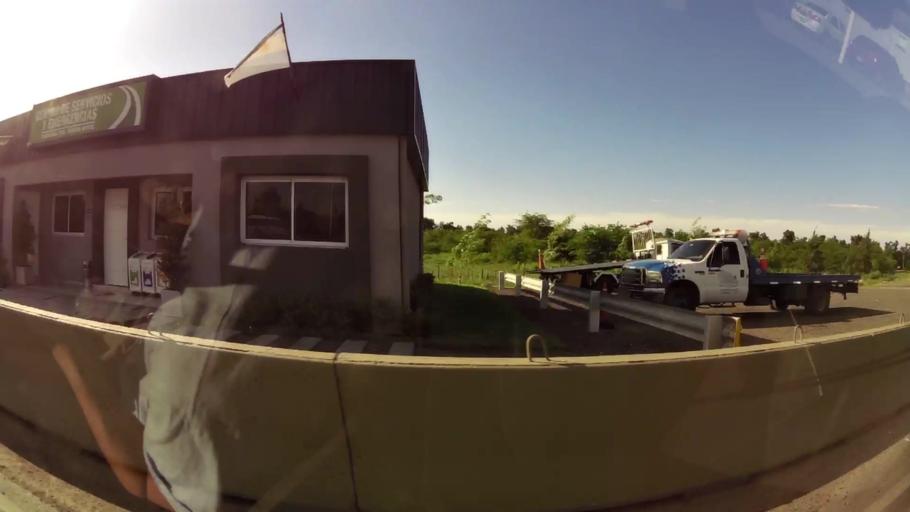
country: AR
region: Buenos Aires
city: Hurlingham
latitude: -34.5654
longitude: -58.6326
